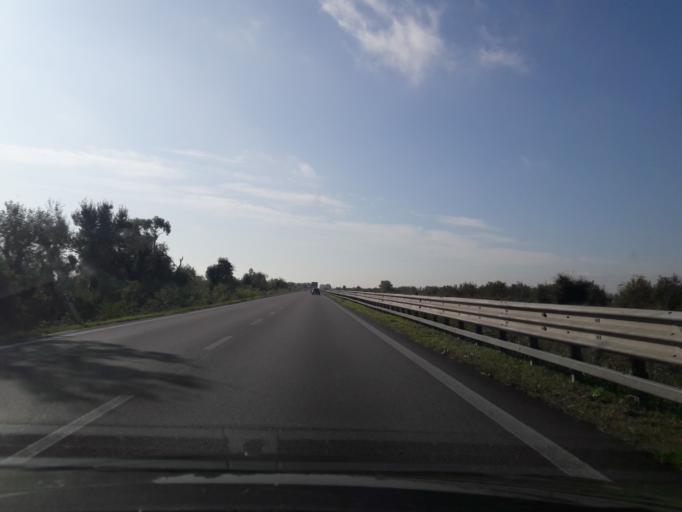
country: IT
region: Veneto
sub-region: Provincia di Venezia
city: Campagna Lupia
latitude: 45.3587
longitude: 12.1369
